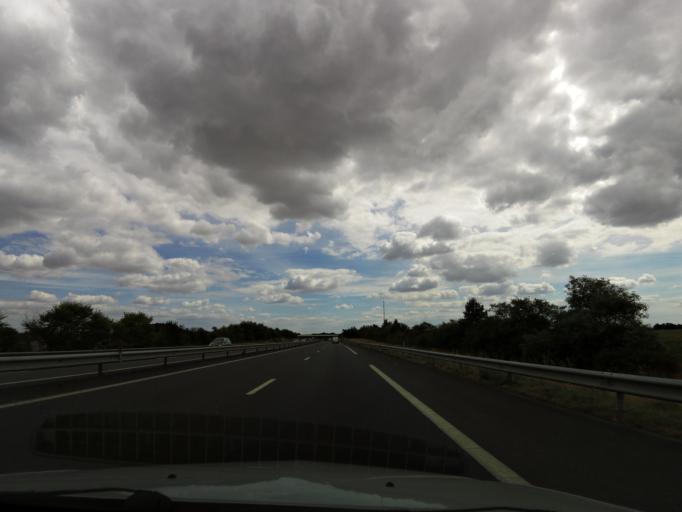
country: FR
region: Pays de la Loire
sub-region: Departement de la Loire-Atlantique
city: La Planche
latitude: 47.0330
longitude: -1.4072
